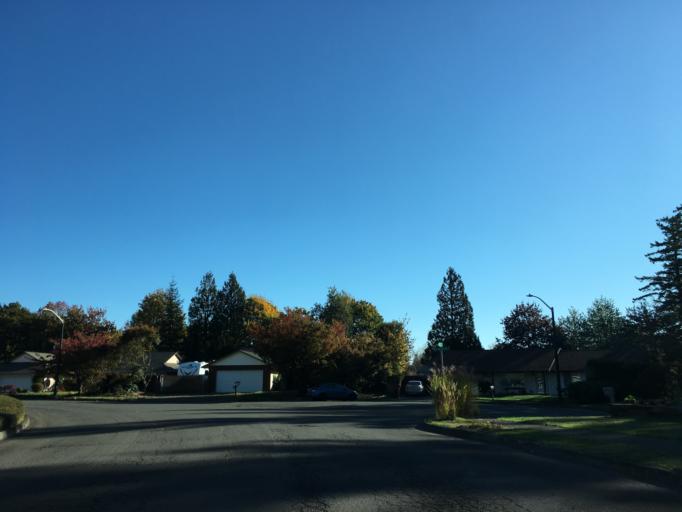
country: US
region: Oregon
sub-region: Multnomah County
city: Wood Village
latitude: 45.5148
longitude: -122.4181
